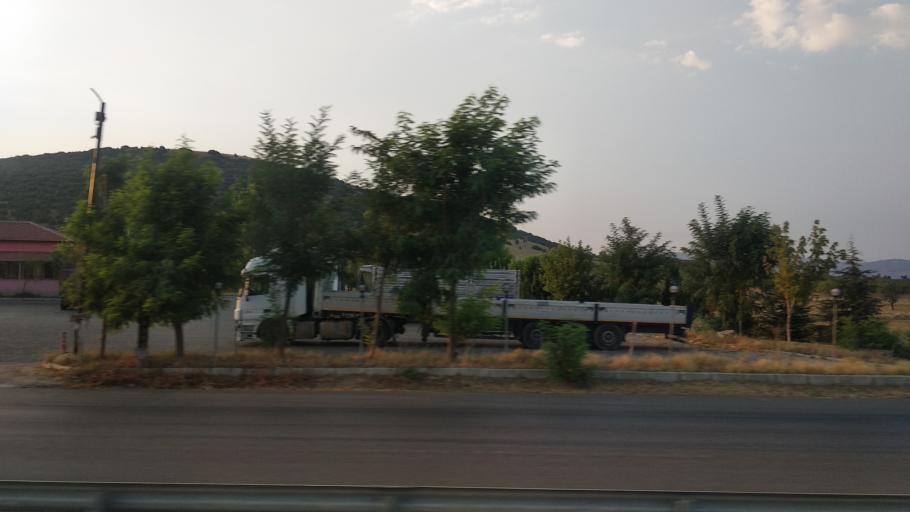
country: TR
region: Manisa
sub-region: Kula
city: Kula
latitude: 38.5578
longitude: 28.6998
